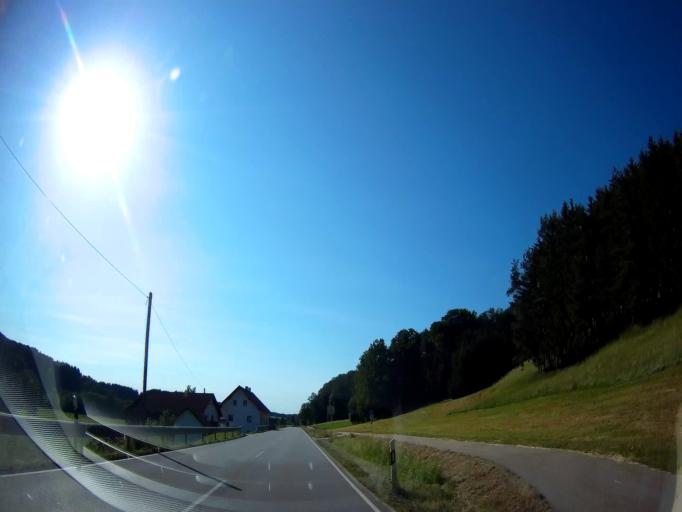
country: DE
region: Bavaria
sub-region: Upper Bavaria
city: Stammham
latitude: 48.2723
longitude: 12.8805
